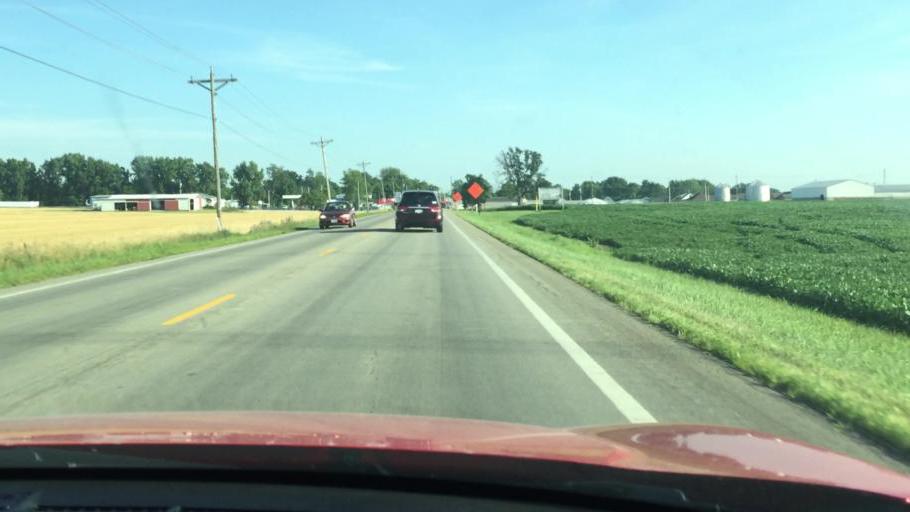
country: US
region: Ohio
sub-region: Logan County
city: Northwood
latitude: 40.4511
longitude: -83.8074
